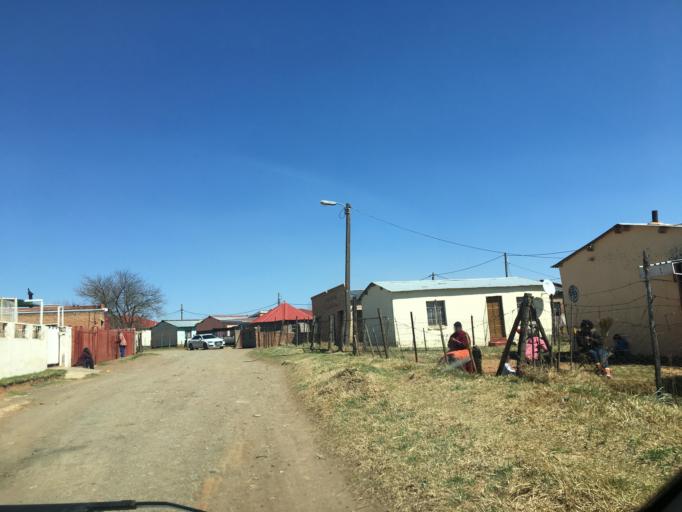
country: ZA
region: Eastern Cape
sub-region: Chris Hani District Municipality
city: Elliot
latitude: -31.3288
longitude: 27.8234
